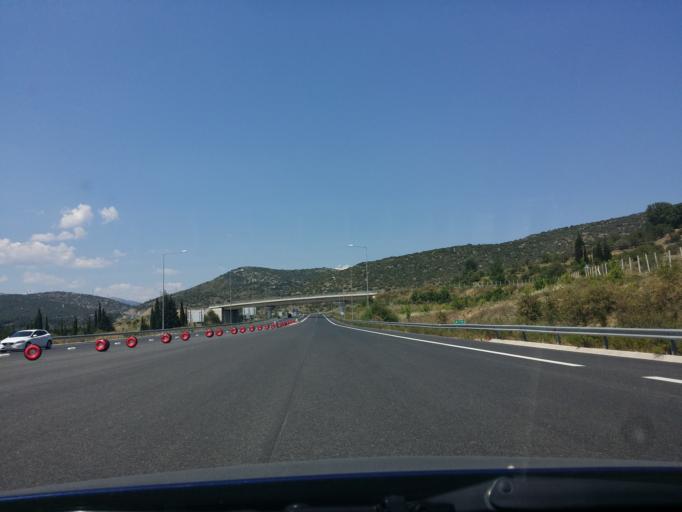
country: GR
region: Peloponnese
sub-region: Nomos Arkadias
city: Tripoli
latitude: 37.4140
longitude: 22.3083
